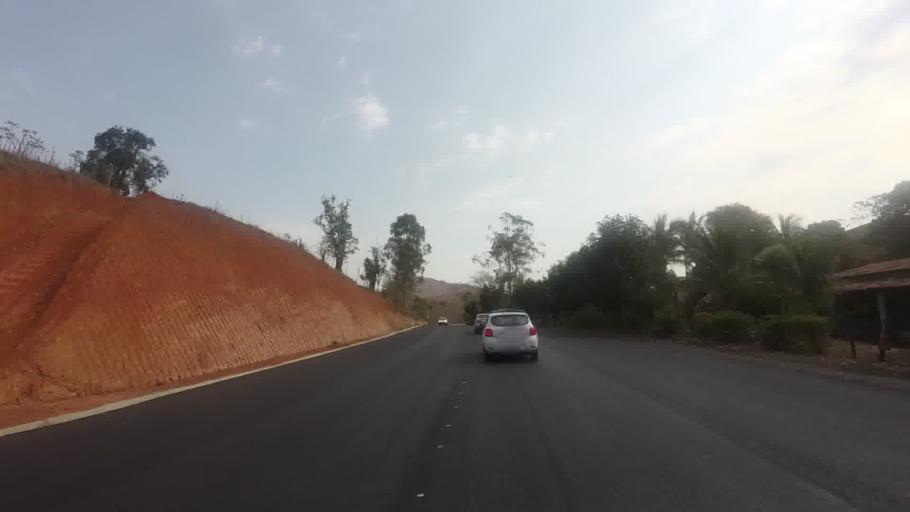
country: BR
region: Rio de Janeiro
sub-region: Bom Jesus Do Itabapoana
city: Bom Jesus do Itabapoana
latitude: -21.1992
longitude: -41.7150
